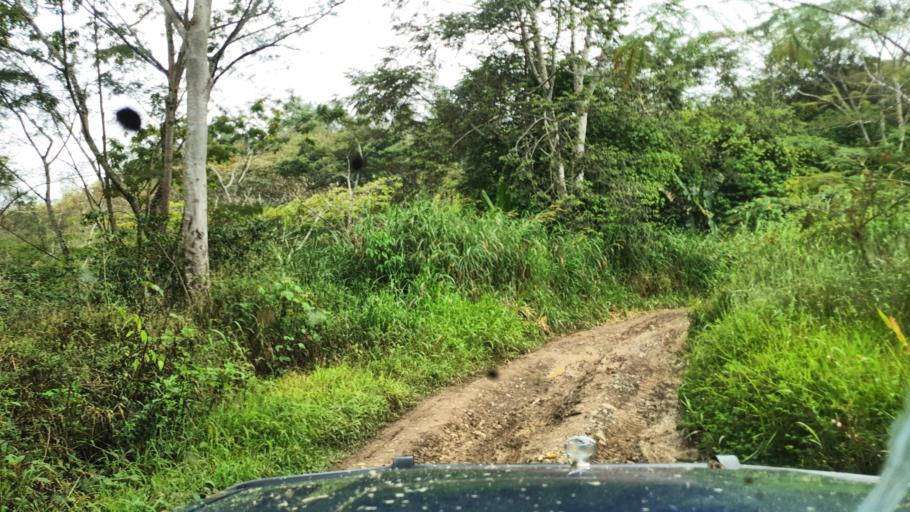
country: PG
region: Jiwaka
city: Minj
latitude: -5.9267
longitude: 144.7425
